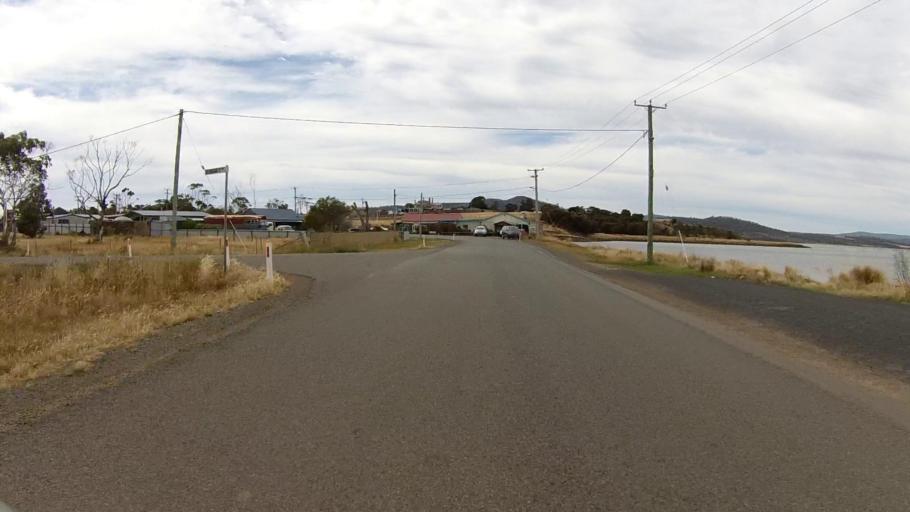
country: AU
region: Tasmania
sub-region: Sorell
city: Sorell
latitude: -42.8925
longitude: 147.8007
